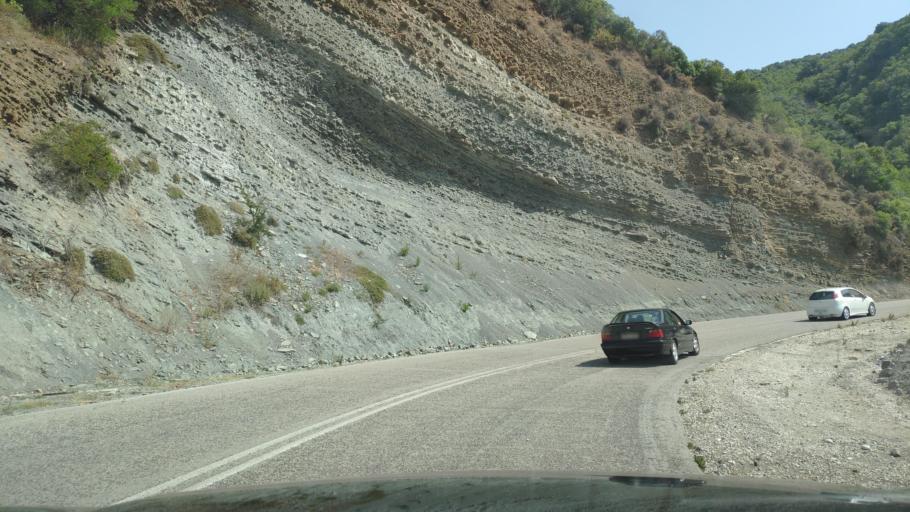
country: GR
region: Epirus
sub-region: Nomos Artas
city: Peta
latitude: 39.1705
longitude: 21.0611
